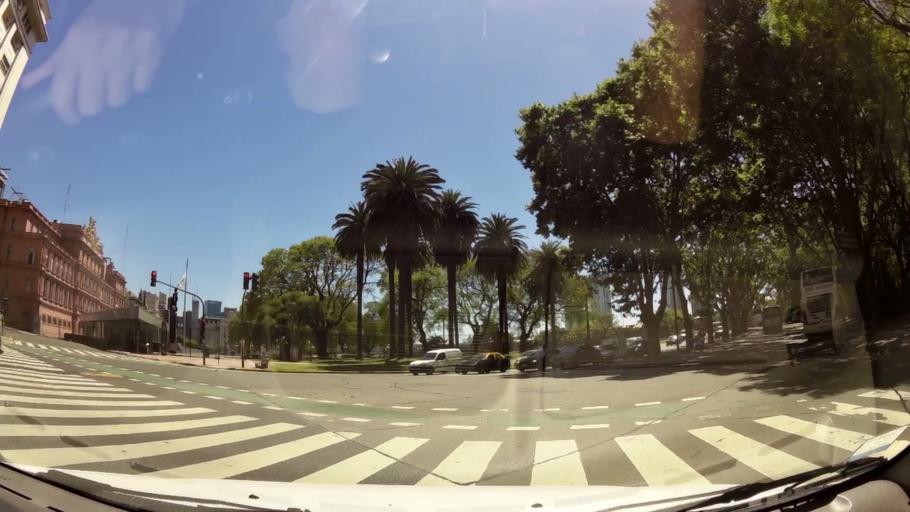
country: AR
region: Buenos Aires F.D.
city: Buenos Aires
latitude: -34.6095
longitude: -58.3694
